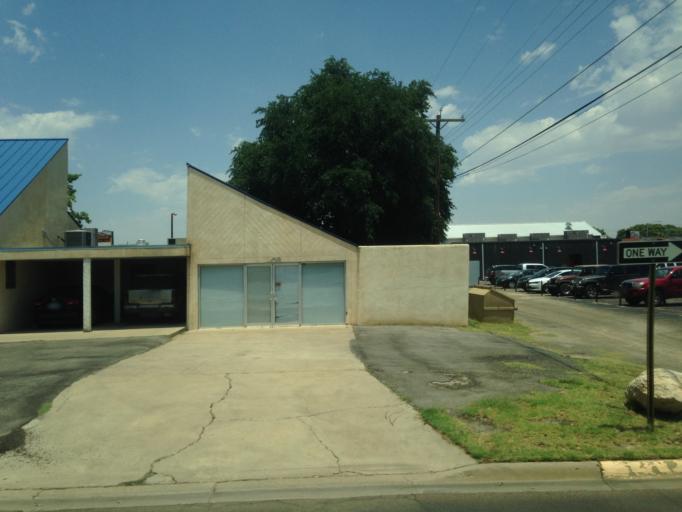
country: US
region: Texas
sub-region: Midland County
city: Midland
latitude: 32.0026
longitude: -102.0779
